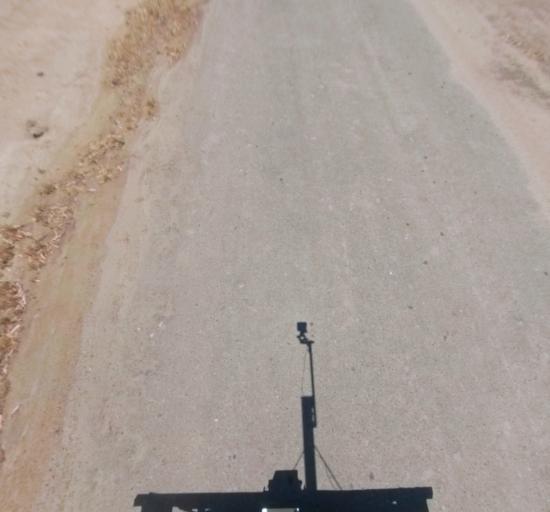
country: US
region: California
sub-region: Madera County
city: Chowchilla
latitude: 37.0565
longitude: -120.2660
